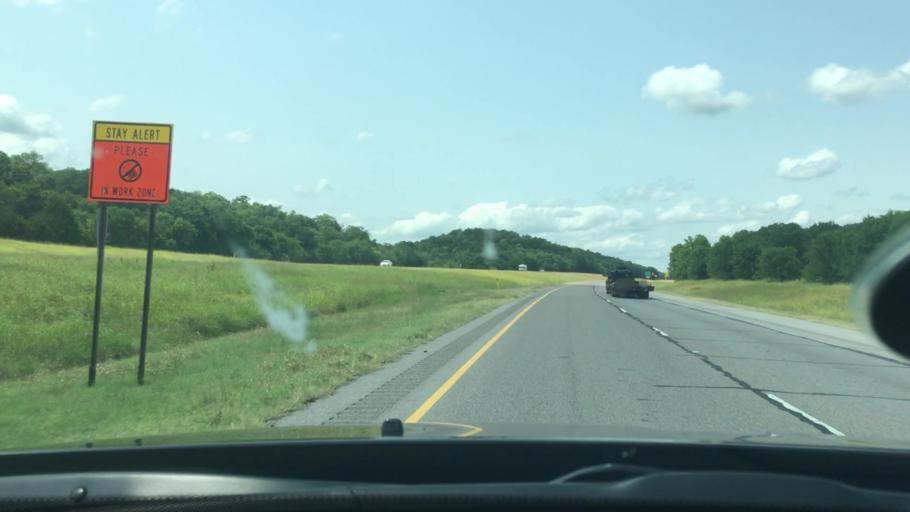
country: US
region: Oklahoma
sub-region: Murray County
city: Davis
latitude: 34.4692
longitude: -97.1526
